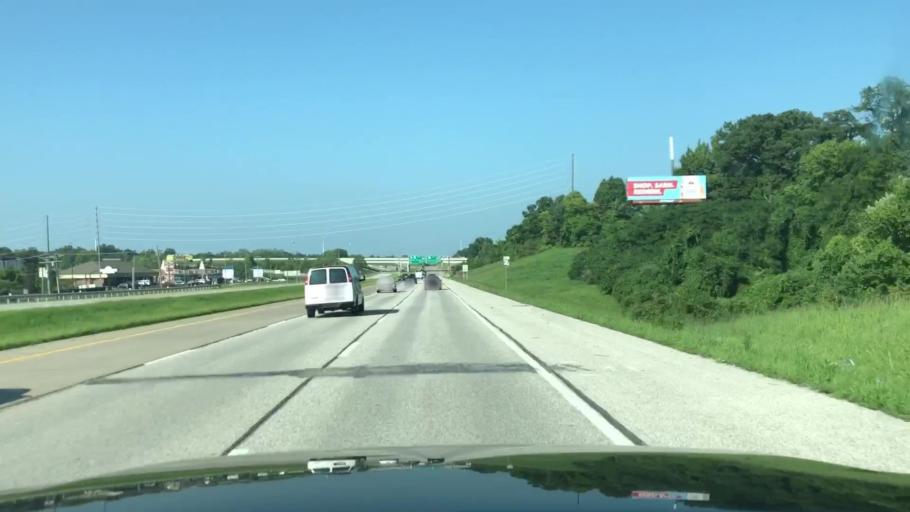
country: US
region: Missouri
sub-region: Saint Charles County
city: Saint Charles
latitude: 38.7589
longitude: -90.5367
